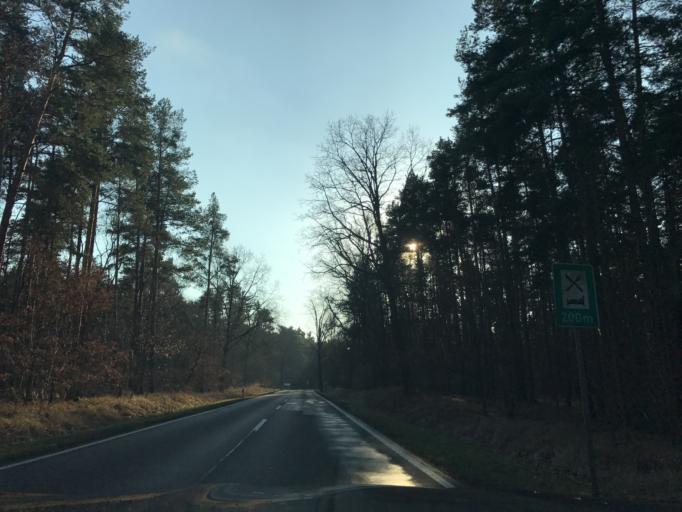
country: DE
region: Brandenburg
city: Wenzlow
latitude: 52.3494
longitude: 12.5009
